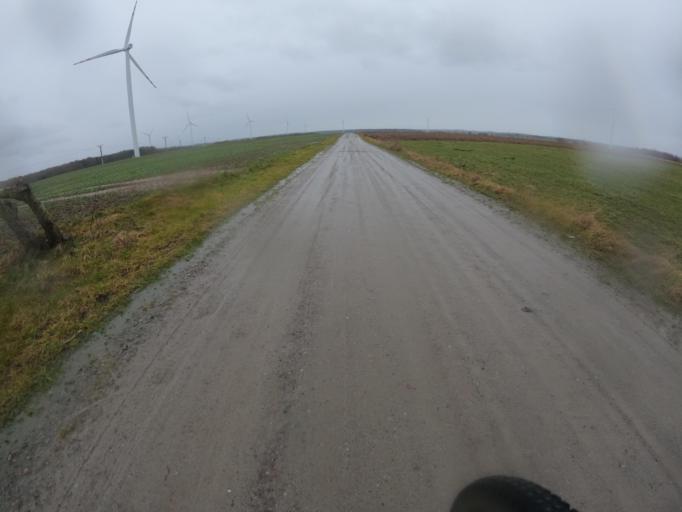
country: PL
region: West Pomeranian Voivodeship
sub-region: Powiat slawienski
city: Darlowo
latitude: 54.4005
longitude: 16.5297
